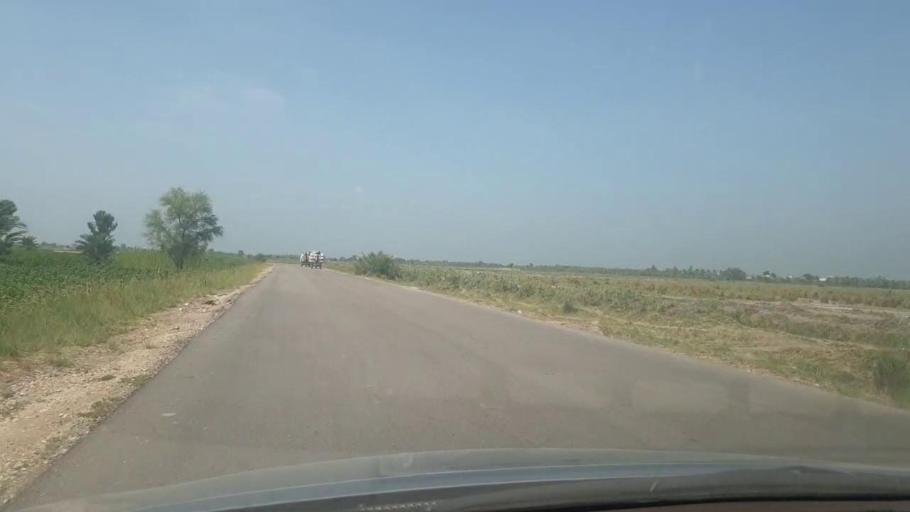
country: PK
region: Sindh
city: Ranipur
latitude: 27.2406
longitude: 68.5735
